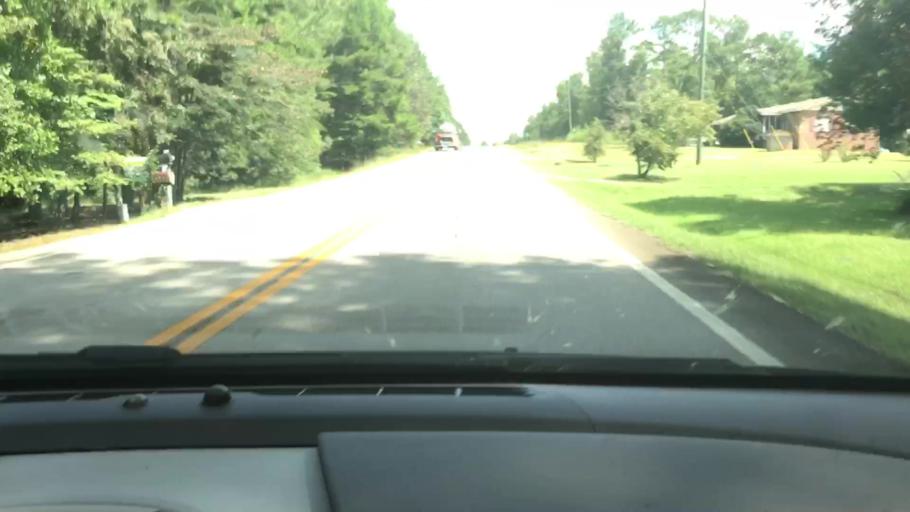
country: US
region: Georgia
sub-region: Troup County
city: La Grange
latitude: 32.9095
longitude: -85.0229
